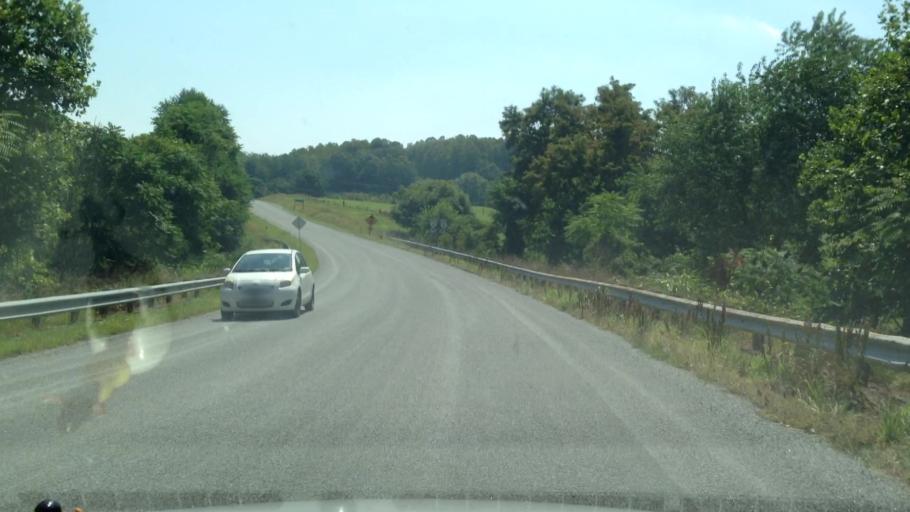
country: US
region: Virginia
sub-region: Patrick County
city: Stuart
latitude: 36.5887
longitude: -80.2839
